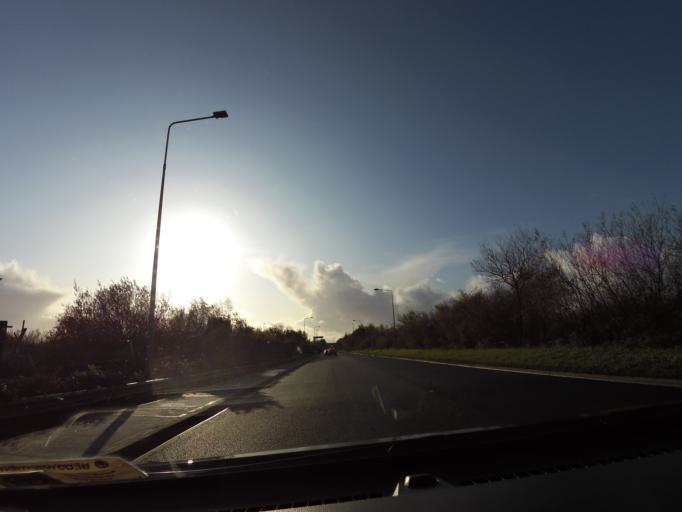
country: IE
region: Munster
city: Moyross
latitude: 52.6480
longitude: -8.6665
